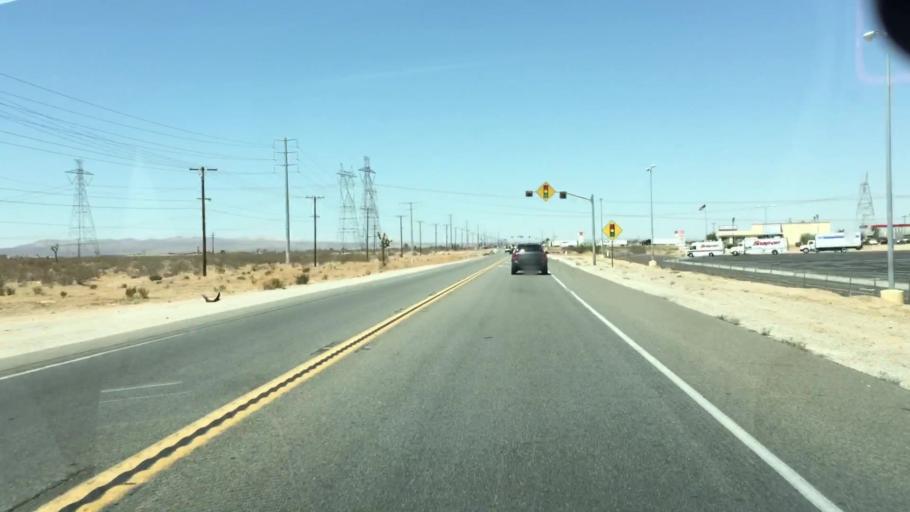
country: US
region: California
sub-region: San Bernardino County
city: Adelanto
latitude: 34.5542
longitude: -117.4035
